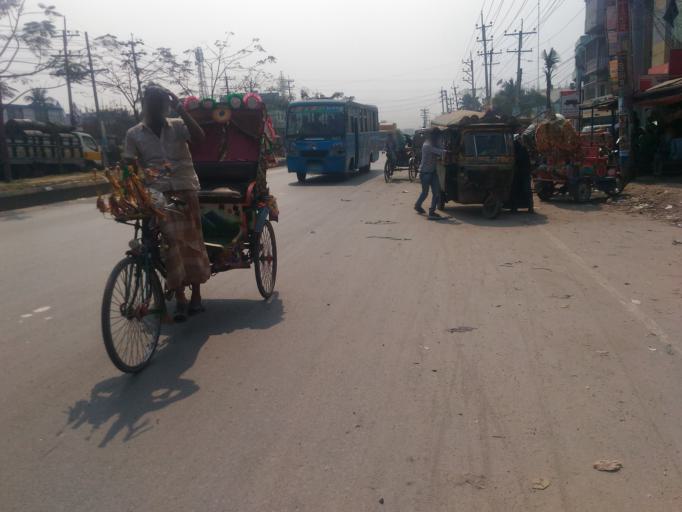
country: BD
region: Dhaka
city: Tungi
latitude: 24.0003
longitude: 90.3826
